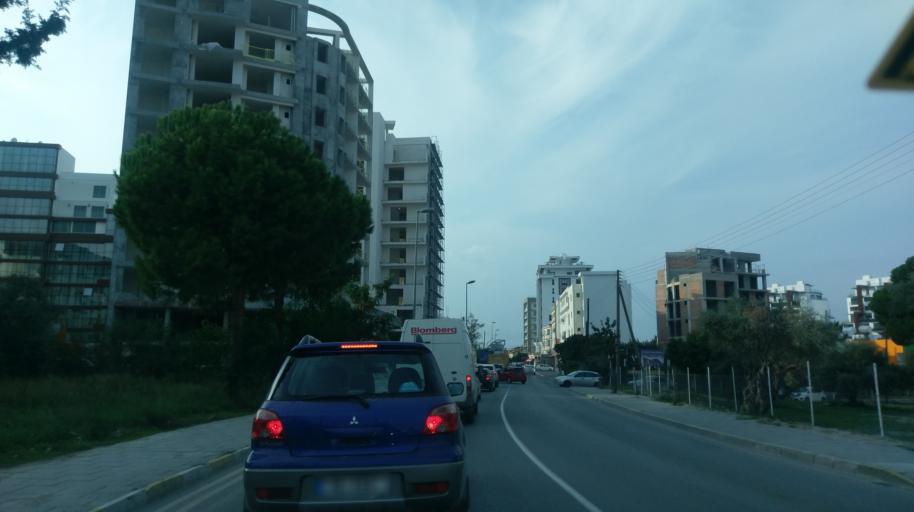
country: CY
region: Keryneia
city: Kyrenia
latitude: 35.3302
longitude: 33.3246
